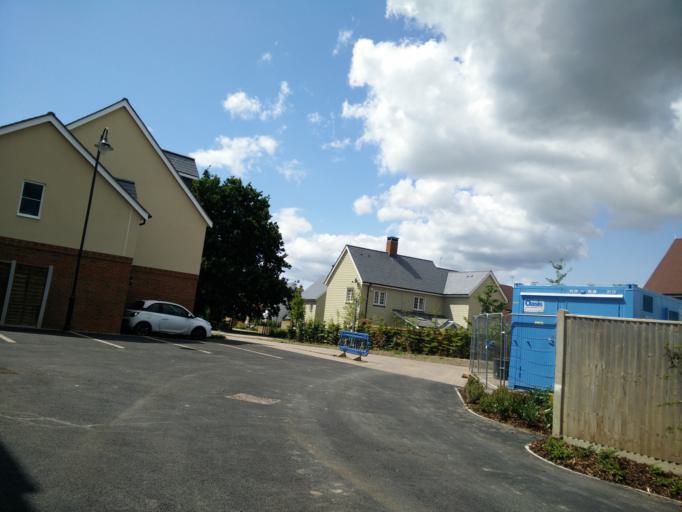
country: GB
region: England
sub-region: West Sussex
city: Horsham
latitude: 51.0632
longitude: -0.3668
